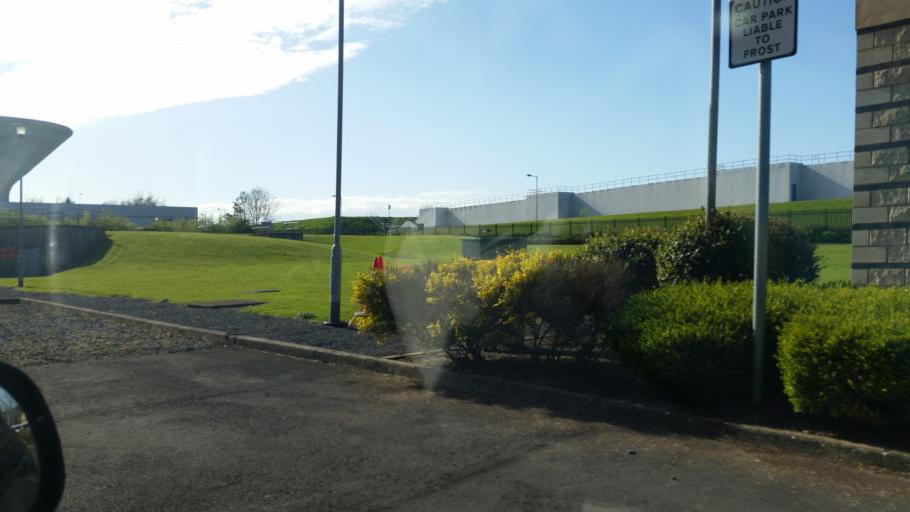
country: IE
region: Leinster
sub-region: Fingal County
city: Blanchardstown
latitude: 53.4096
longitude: -6.3613
